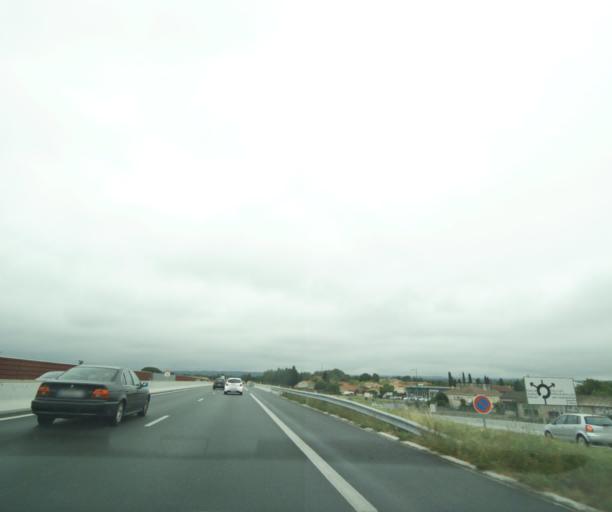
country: FR
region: Midi-Pyrenees
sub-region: Departement du Tarn
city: Puygouzon
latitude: 43.9203
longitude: 2.1675
